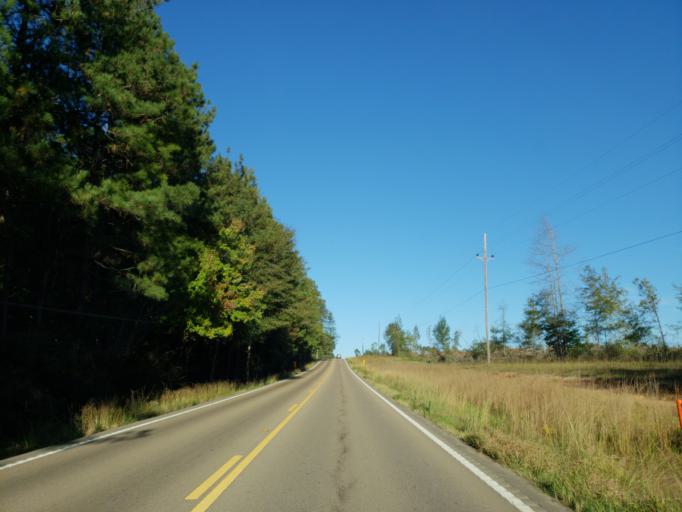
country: US
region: Mississippi
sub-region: Perry County
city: Richton
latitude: 31.3600
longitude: -88.9006
